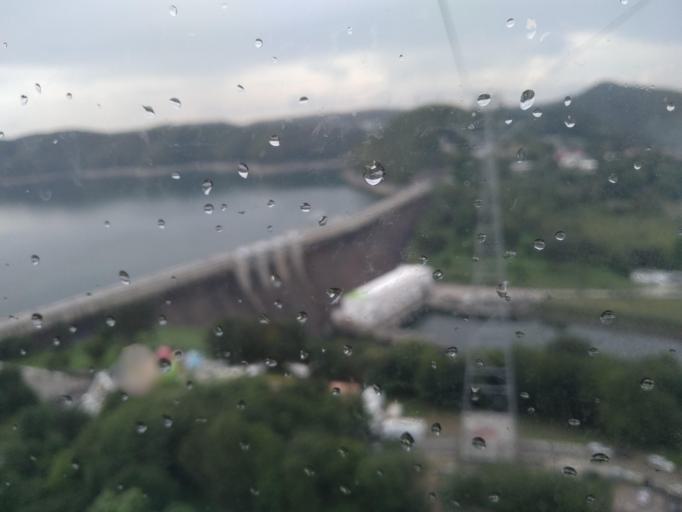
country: PL
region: Subcarpathian Voivodeship
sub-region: Powiat leski
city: Polanczyk
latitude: 49.3950
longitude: 22.4593
